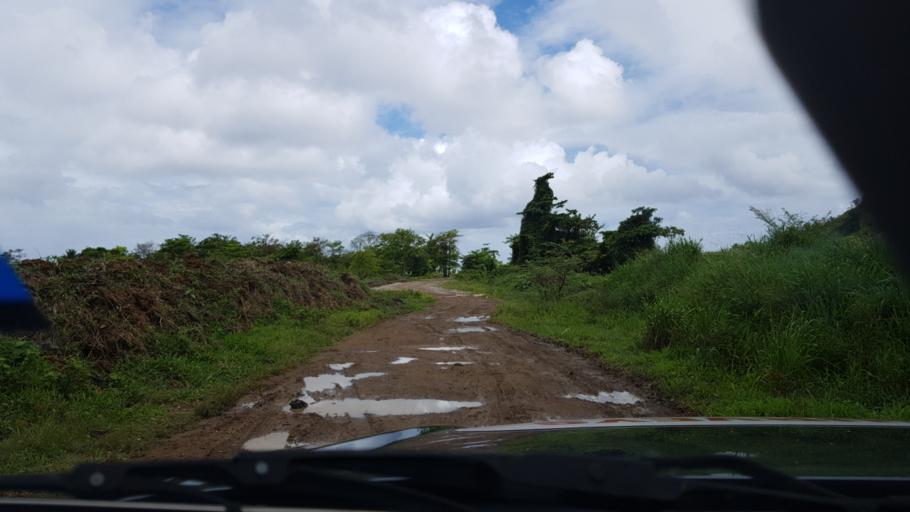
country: LC
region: Anse-la-Raye
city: Anse La Raye
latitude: 13.9553
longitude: -61.0317
